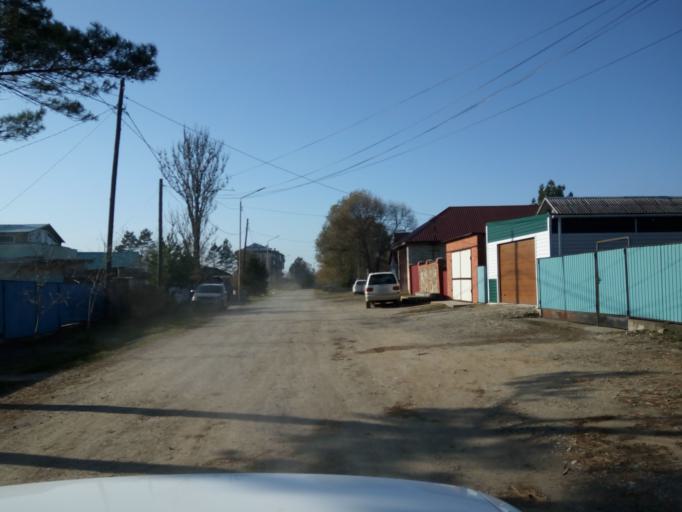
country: RU
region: Primorskiy
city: Dal'nerechensk
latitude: 45.9209
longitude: 133.7445
